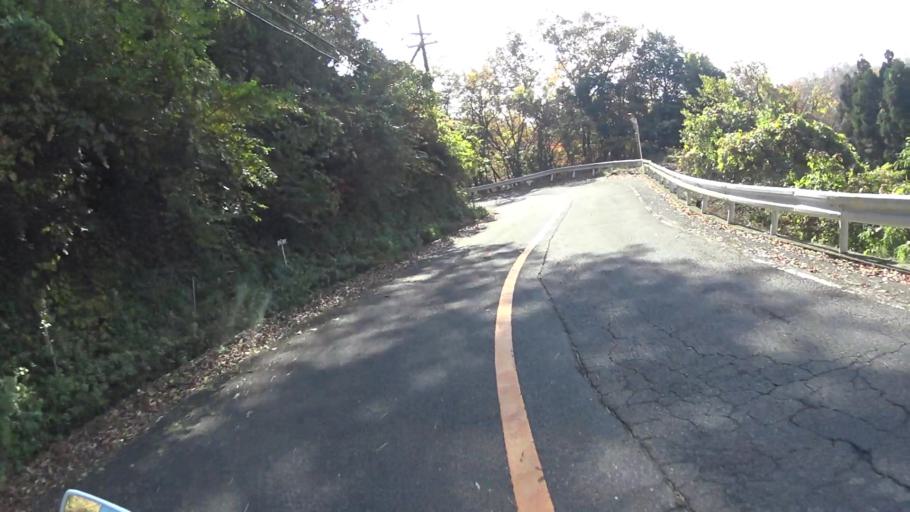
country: JP
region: Kyoto
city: Maizuru
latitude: 35.4627
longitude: 135.3535
